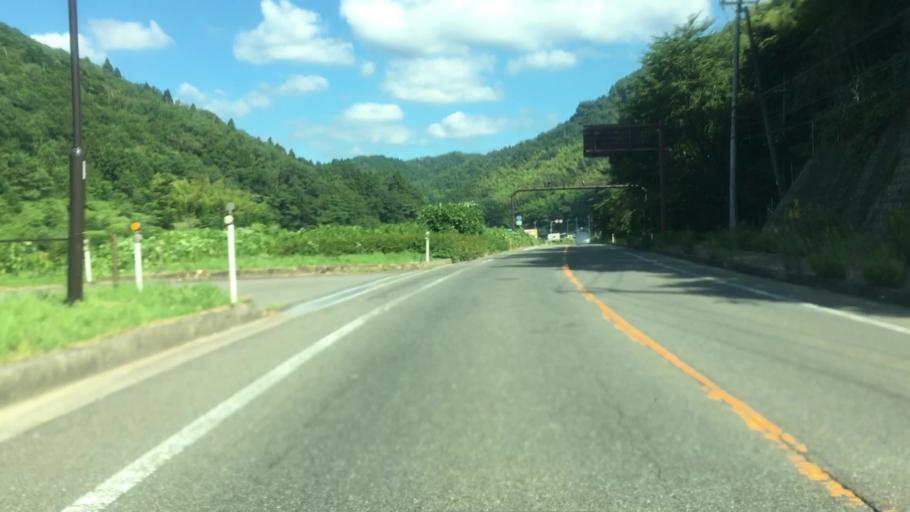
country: JP
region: Hyogo
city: Toyooka
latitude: 35.5672
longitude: 134.7831
